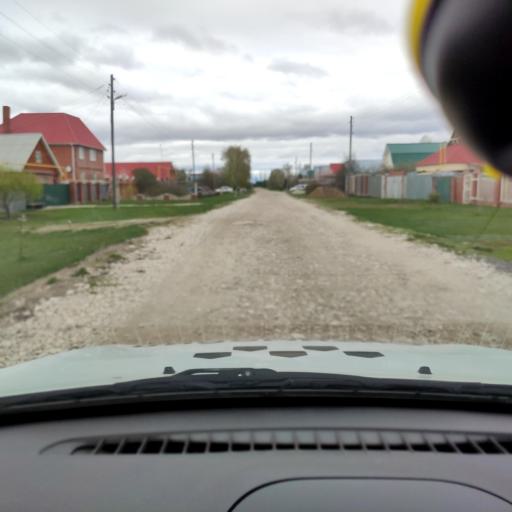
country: RU
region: Samara
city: Tol'yatti
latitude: 53.5796
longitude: 49.3295
